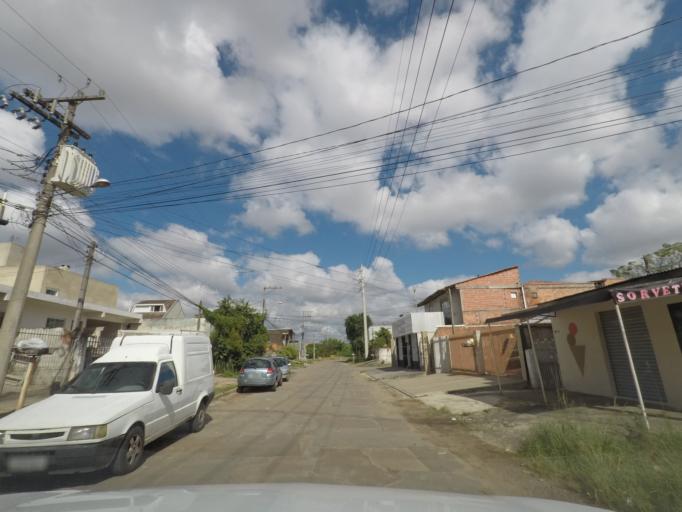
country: BR
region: Parana
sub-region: Sao Jose Dos Pinhais
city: Sao Jose dos Pinhais
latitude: -25.4888
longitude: -49.2303
